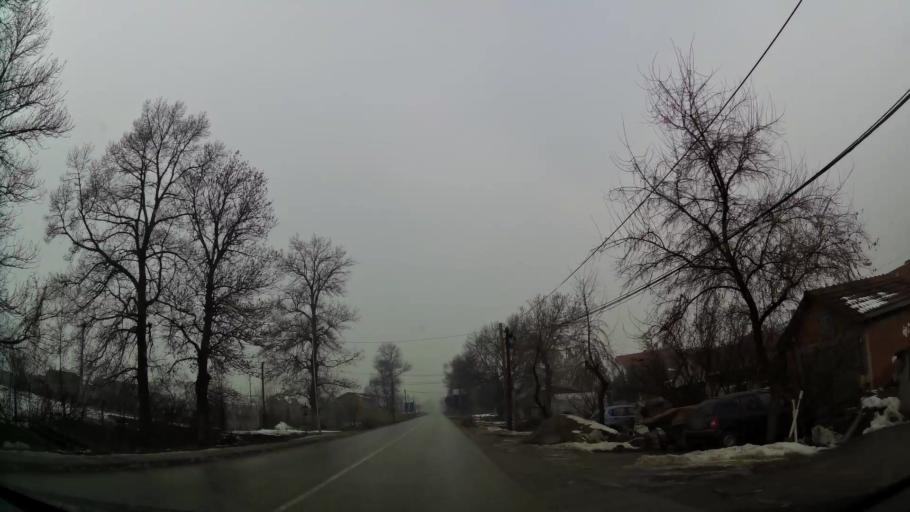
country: MK
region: Petrovec
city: Petrovec
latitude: 41.9416
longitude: 21.6089
